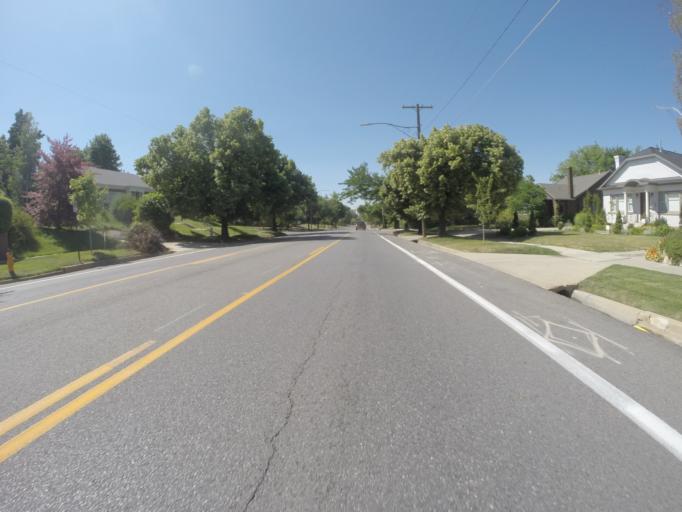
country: US
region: Utah
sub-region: Salt Lake County
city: Salt Lake City
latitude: 40.7481
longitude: -111.8539
